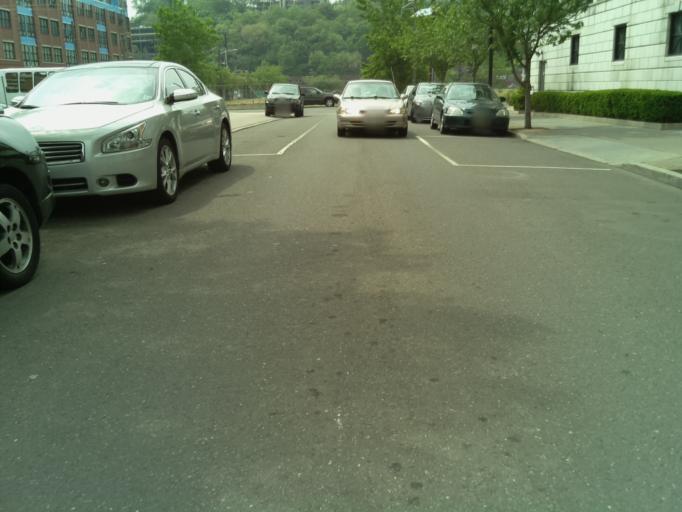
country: US
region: New Jersey
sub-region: Hudson County
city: Hoboken
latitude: 40.7521
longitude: -74.0325
